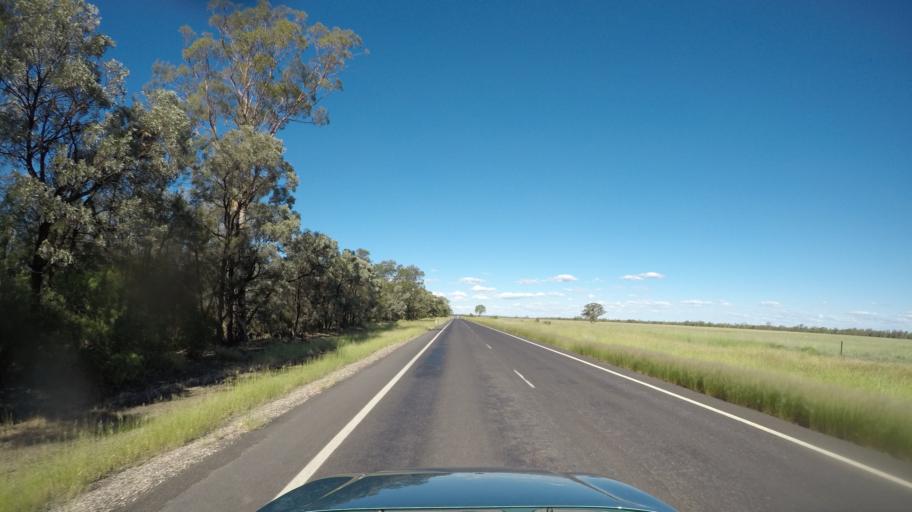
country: AU
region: Queensland
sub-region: Goondiwindi
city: Goondiwindi
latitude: -28.1549
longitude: 150.6734
